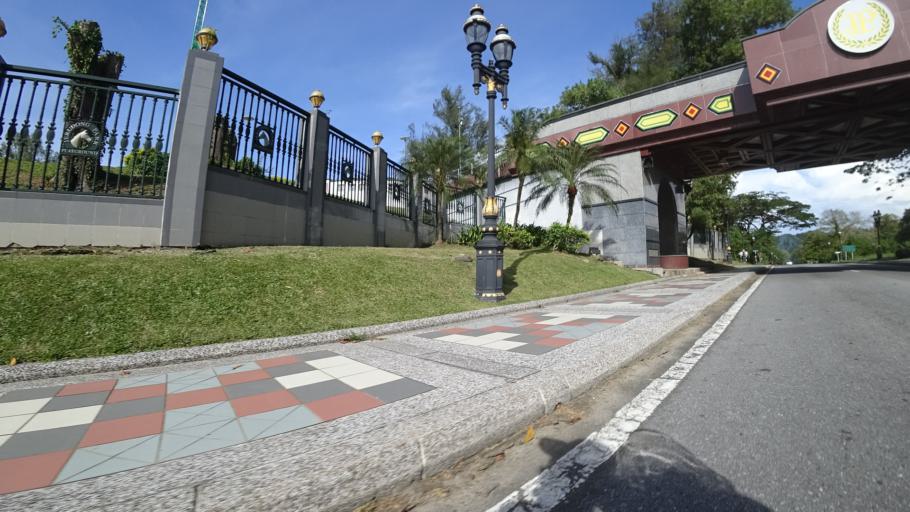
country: BN
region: Brunei and Muara
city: Bandar Seri Begawan
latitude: 4.9370
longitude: 114.8378
